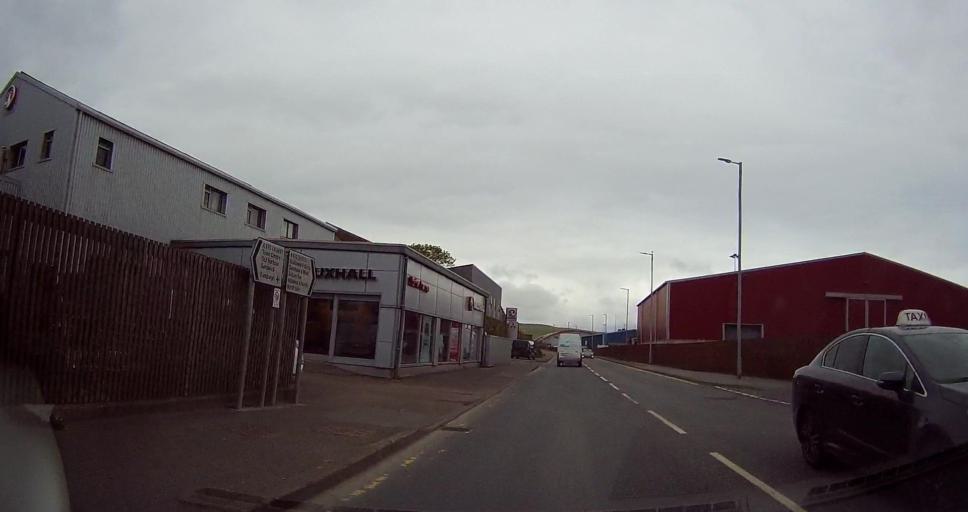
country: GB
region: Scotland
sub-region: Shetland Islands
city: Lerwick
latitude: 60.1596
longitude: -1.1570
